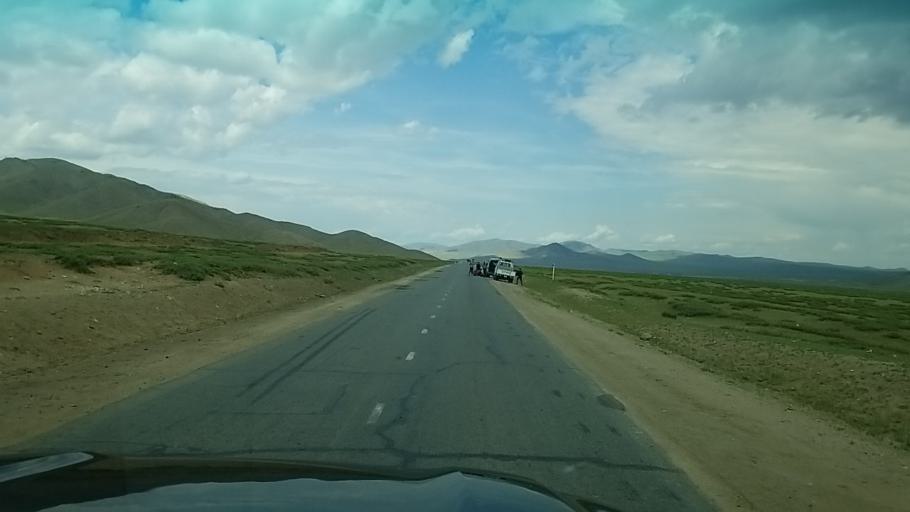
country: MN
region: Darhan Uul
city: Orhon
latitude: 49.7214
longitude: 106.1118
